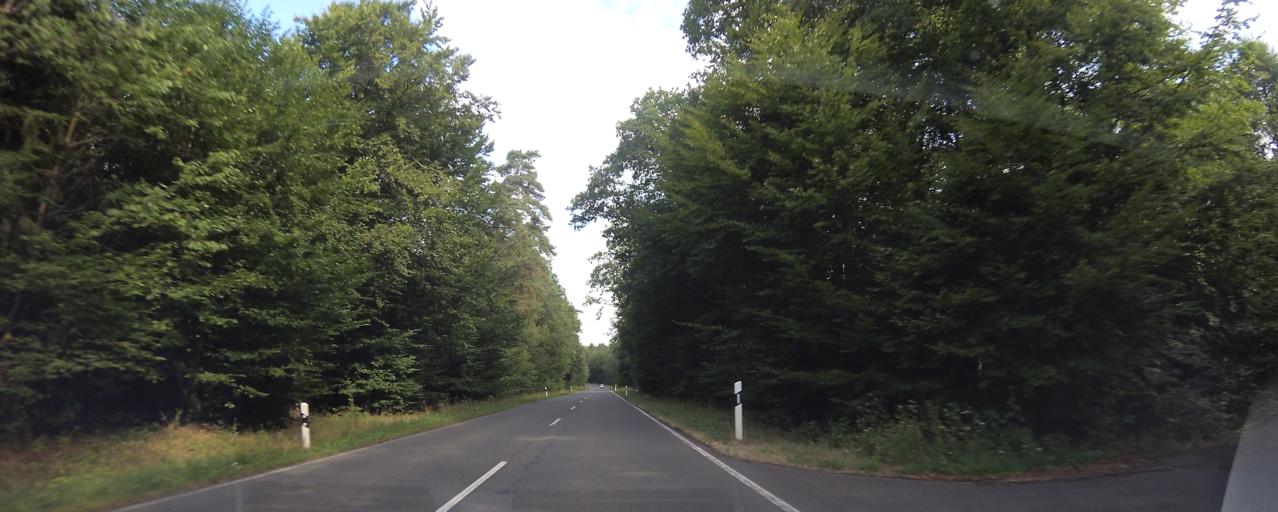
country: DE
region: Rheinland-Pfalz
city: Zemmer
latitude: 49.9195
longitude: 6.7054
